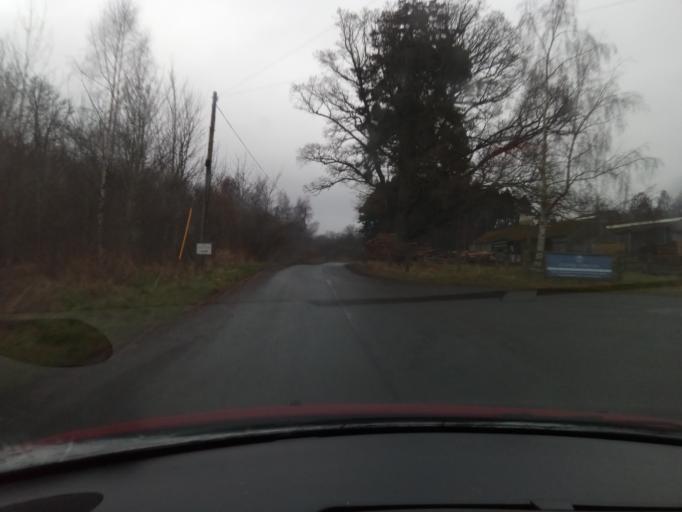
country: GB
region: Scotland
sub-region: The Scottish Borders
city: Kelso
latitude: 55.5519
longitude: -2.4314
